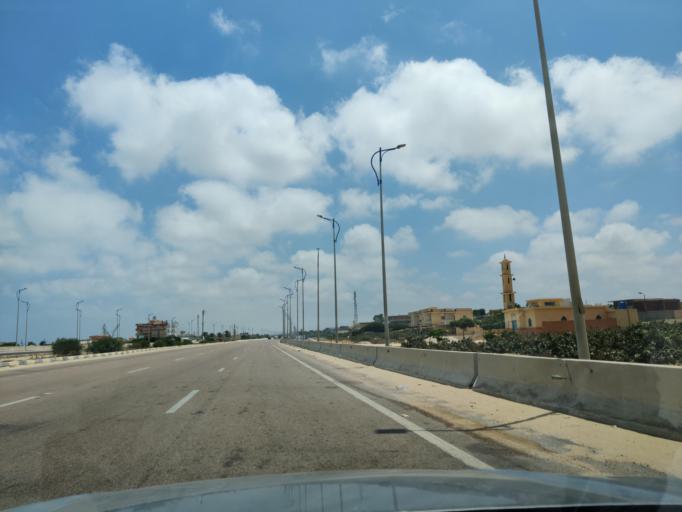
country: EG
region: Alexandria
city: Alexandria
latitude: 30.9643
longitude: 29.5509
